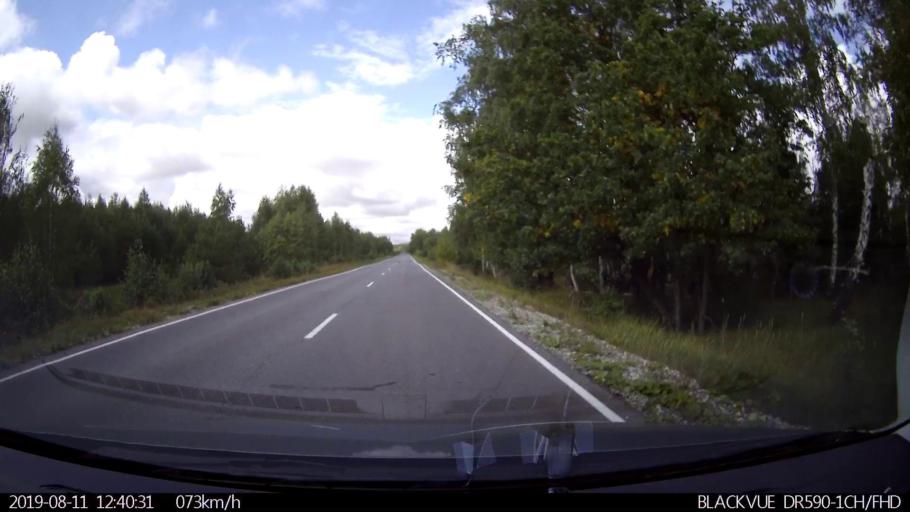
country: RU
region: Ulyanovsk
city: Ignatovka
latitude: 53.8391
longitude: 47.7796
